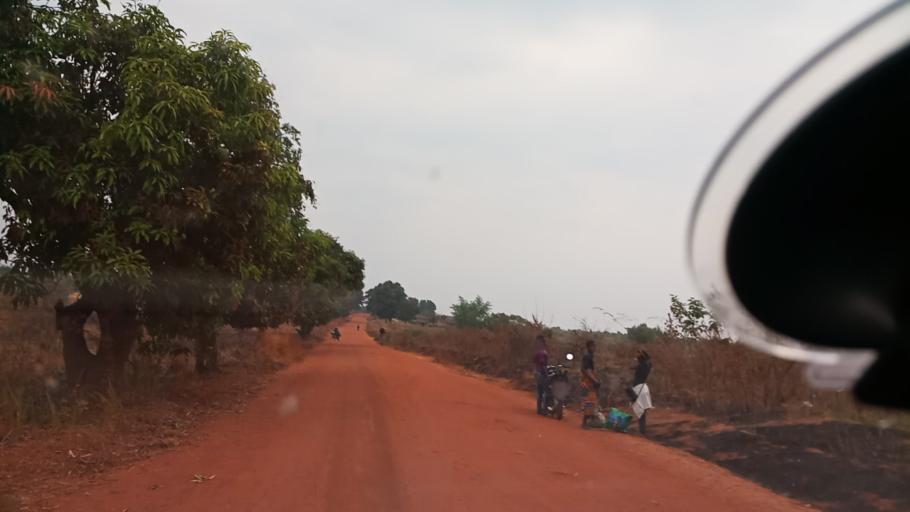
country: ZM
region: Luapula
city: Nchelenge
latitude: -9.1798
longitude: 28.2825
